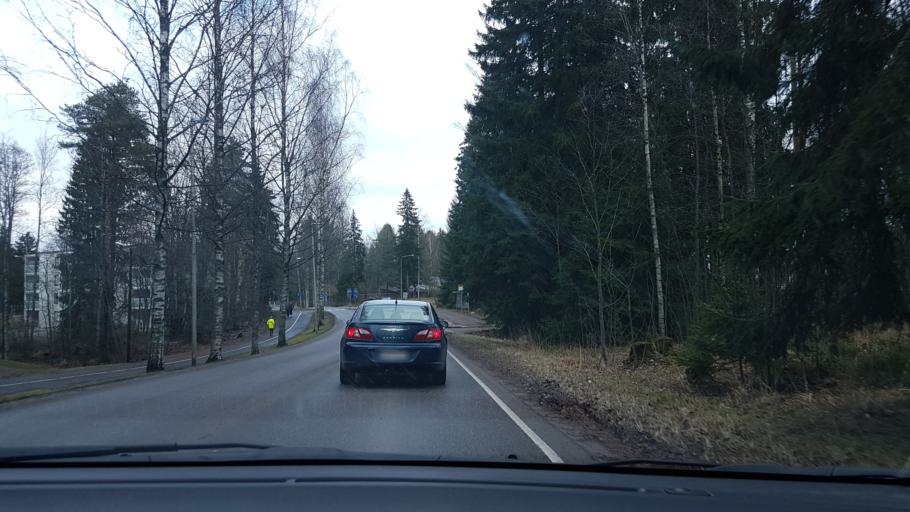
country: FI
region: Uusimaa
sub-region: Helsinki
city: Kerava
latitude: 60.3787
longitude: 25.0852
